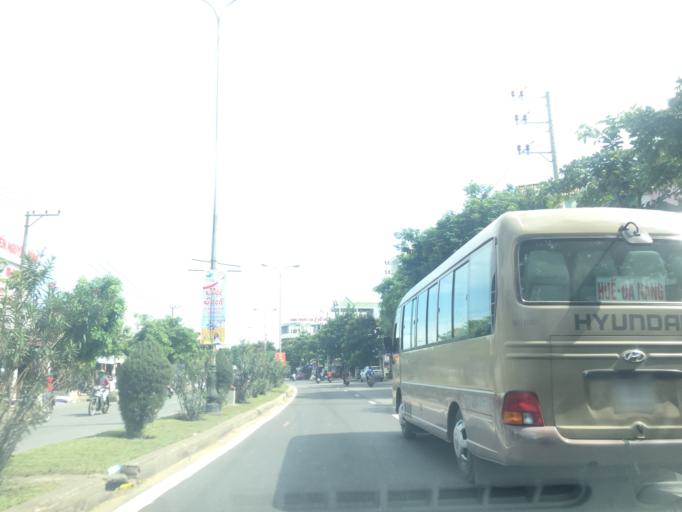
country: VN
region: Da Nang
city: Lien Chieu
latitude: 16.0683
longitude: 108.1519
